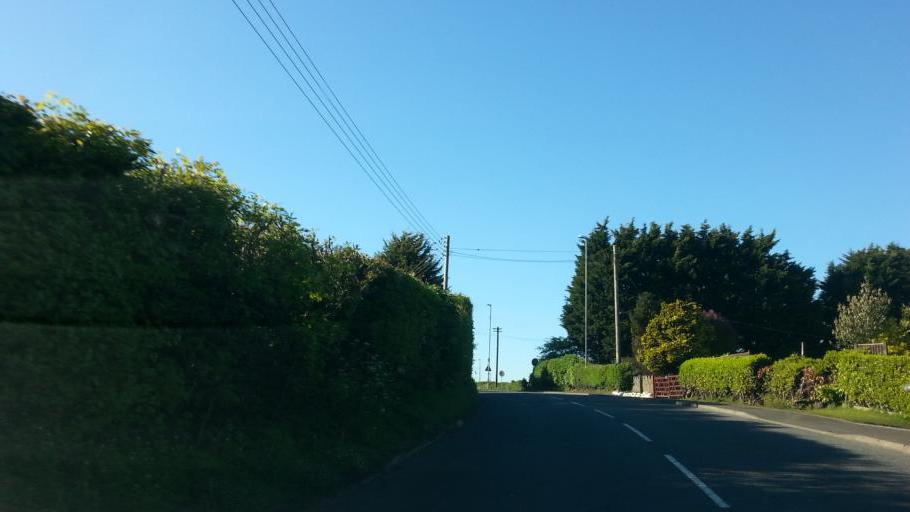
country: GB
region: England
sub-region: Bath and North East Somerset
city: Clutton
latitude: 51.3360
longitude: -2.5485
